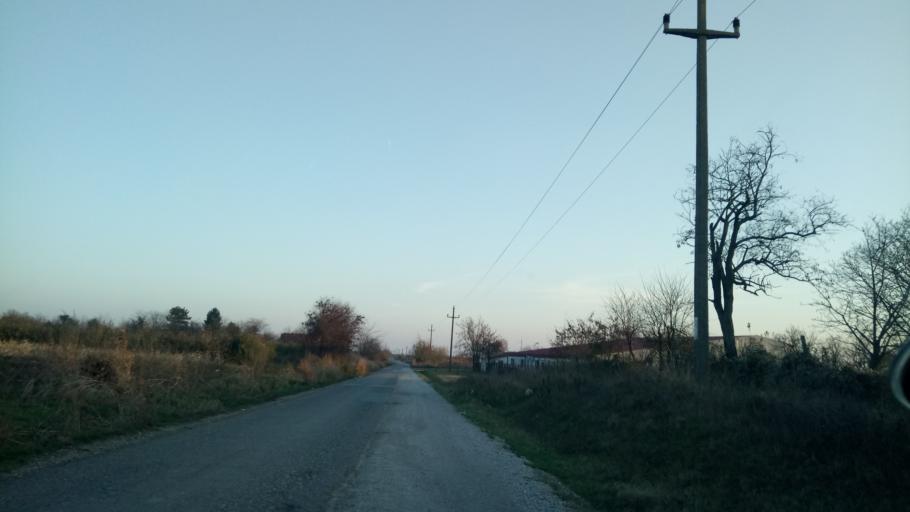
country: RS
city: Novi Slankamen
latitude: 45.1302
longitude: 20.2563
